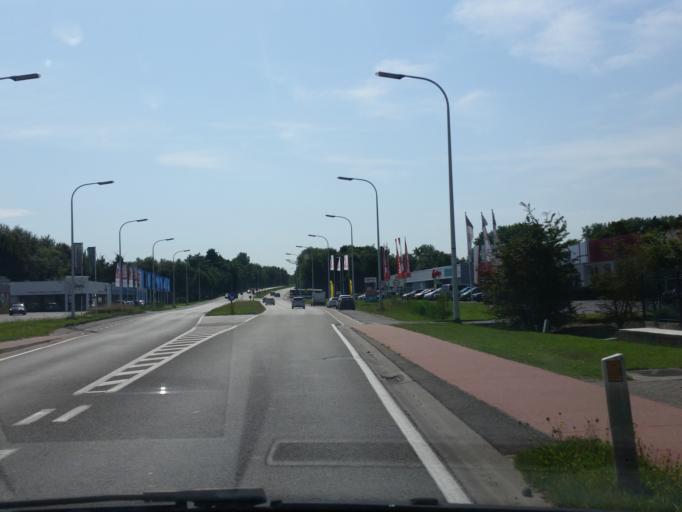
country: BE
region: Flanders
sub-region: Provincie Vlaams-Brabant
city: Zemst
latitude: 50.9949
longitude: 4.4744
